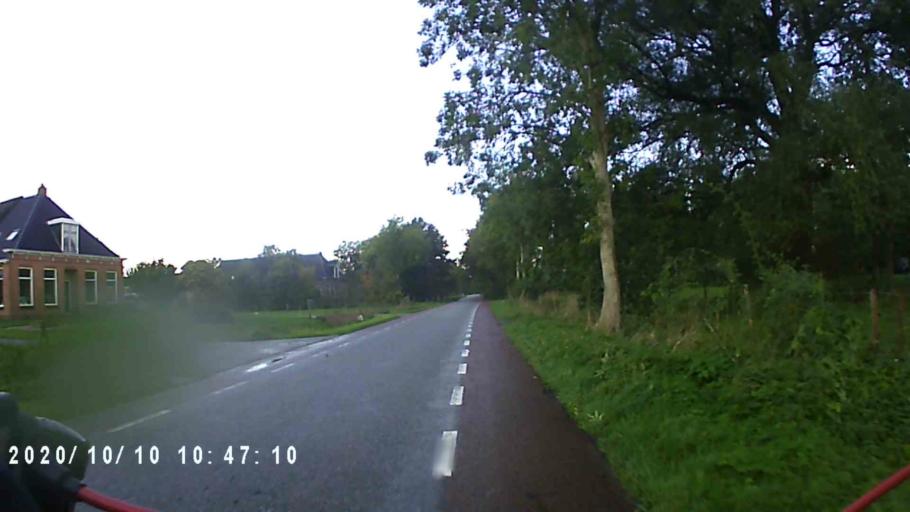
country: NL
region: Groningen
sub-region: Gemeente Grootegast
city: Grootegast
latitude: 53.1668
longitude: 6.2487
